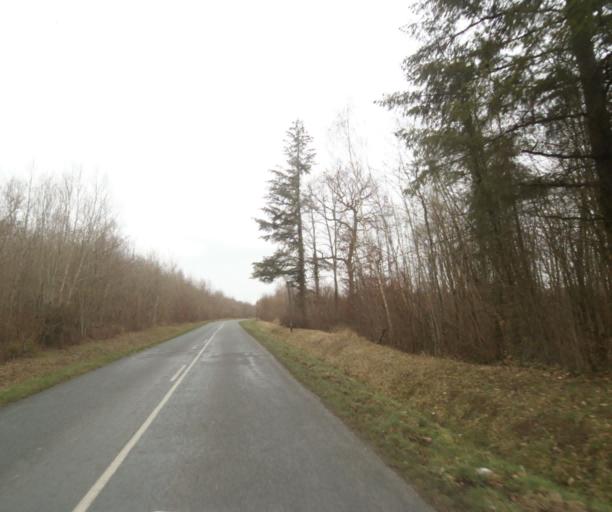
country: FR
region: Champagne-Ardenne
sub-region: Departement de la Haute-Marne
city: Villiers-en-Lieu
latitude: 48.6912
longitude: 4.8900
